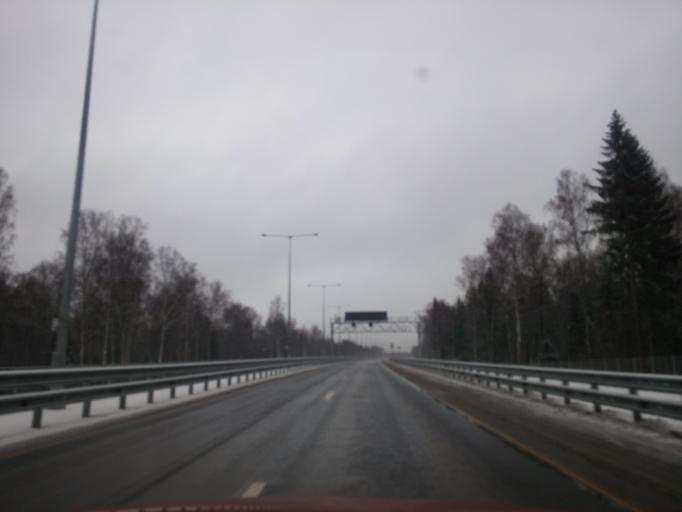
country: RU
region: Tverskaya
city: Likhoslavl'
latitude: 56.9677
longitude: 35.4663
